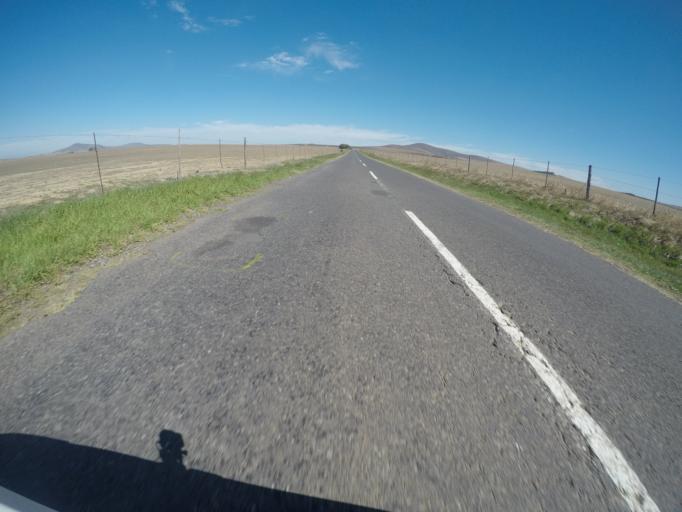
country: ZA
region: Western Cape
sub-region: City of Cape Town
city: Atlantis
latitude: -33.6880
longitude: 18.5971
